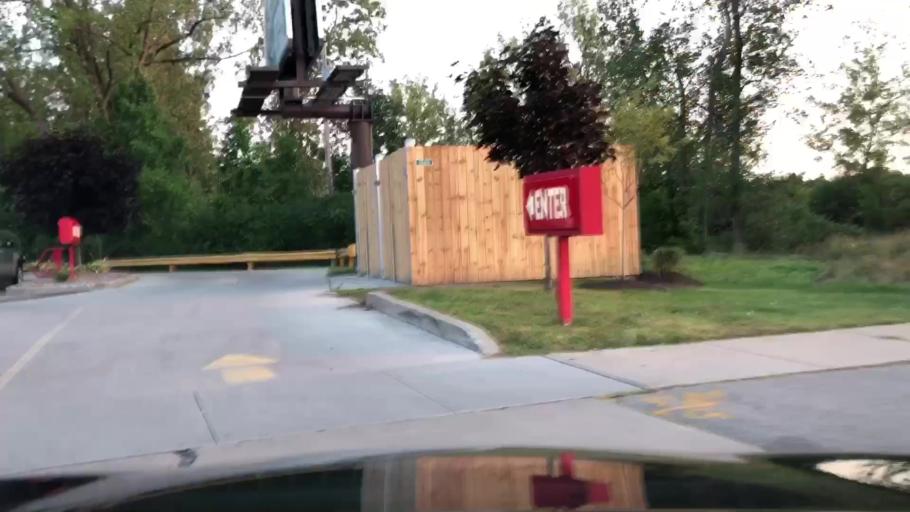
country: US
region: New York
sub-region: Erie County
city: Depew
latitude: 42.8678
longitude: -78.7003
